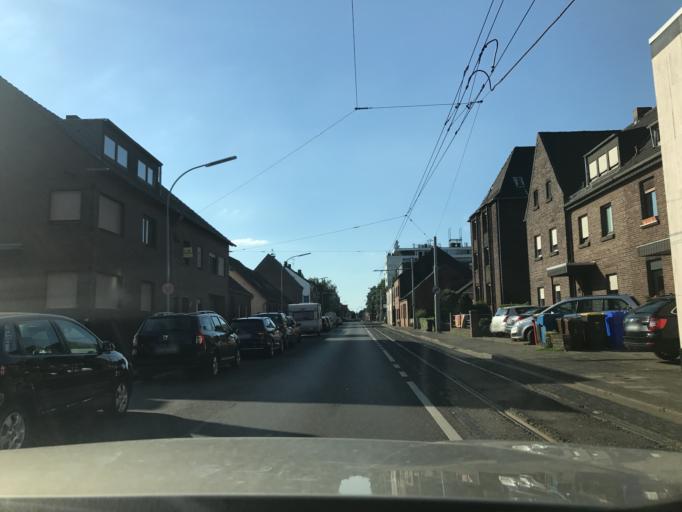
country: DE
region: North Rhine-Westphalia
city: Tonisvorst
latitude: 51.3658
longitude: 6.5167
